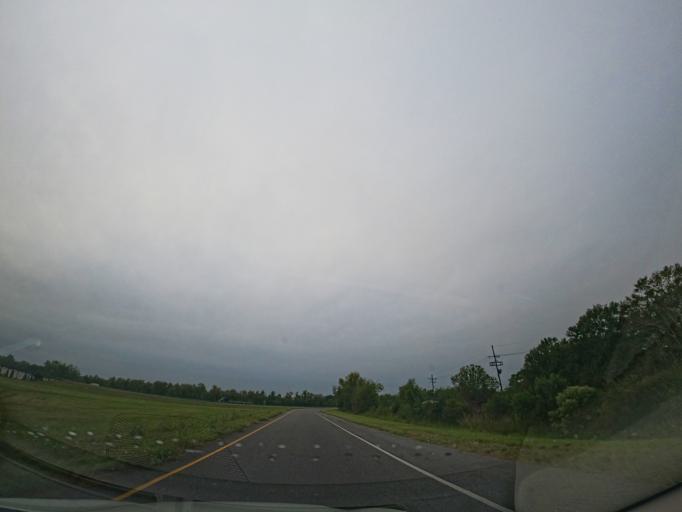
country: US
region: Louisiana
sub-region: Lafourche Parish
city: Raceland
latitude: 29.7064
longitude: -90.5754
